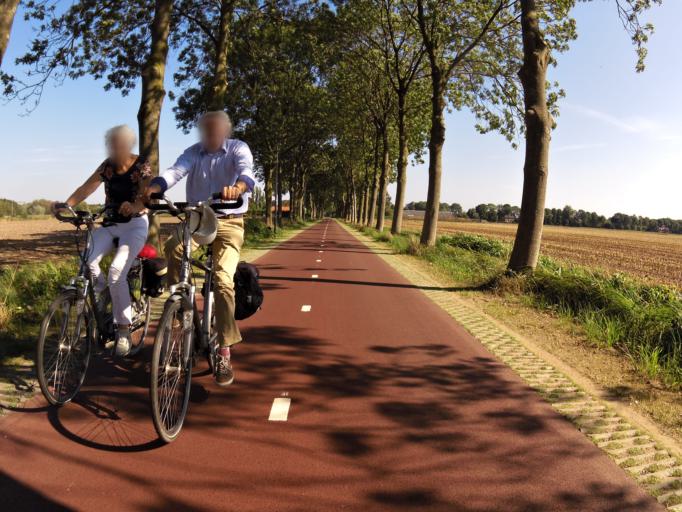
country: NL
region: North Brabant
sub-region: Gemeente Maasdonk
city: Geffen
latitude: 51.7350
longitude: 5.4408
